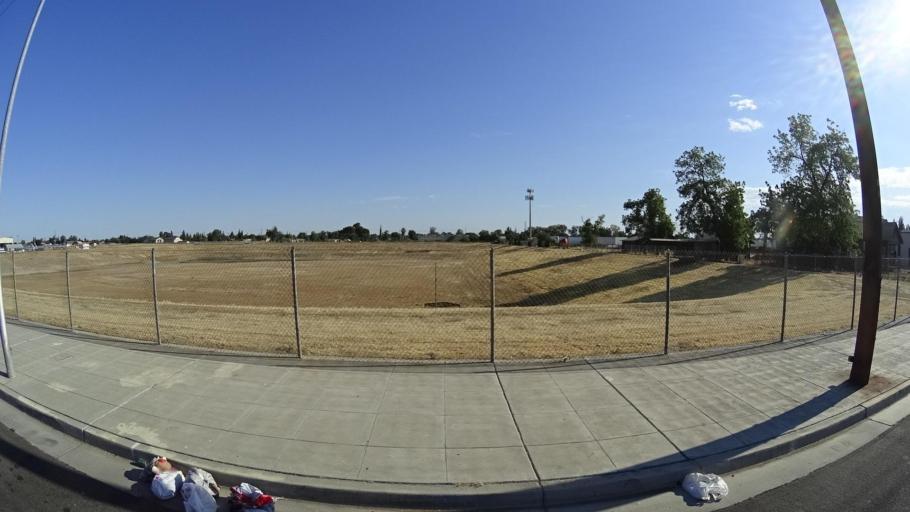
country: US
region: California
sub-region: Fresno County
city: Fresno
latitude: 36.7178
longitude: -119.7483
